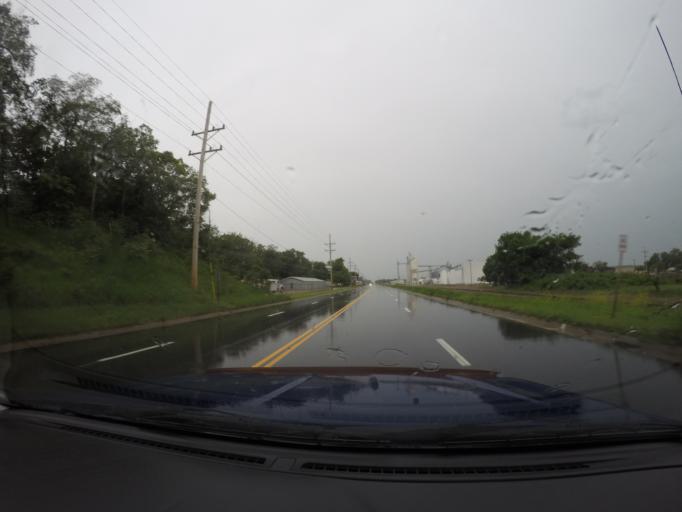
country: US
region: Kansas
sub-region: Cloud County
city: Concordia
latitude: 39.5735
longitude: -97.6685
